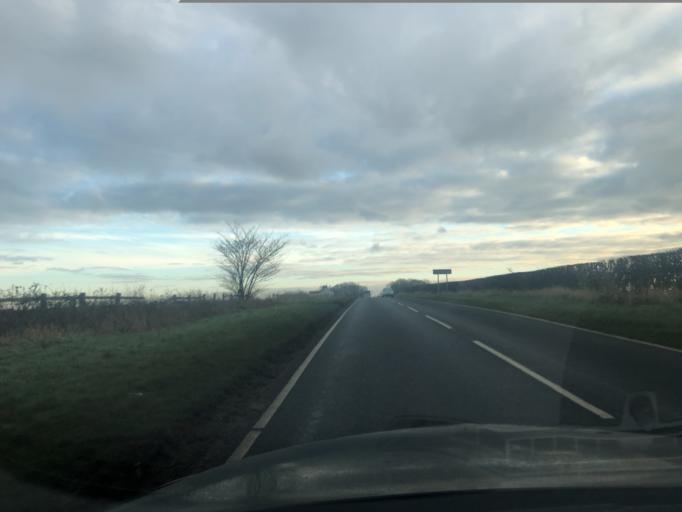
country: GB
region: England
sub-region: North Yorkshire
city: Northallerton
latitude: 54.3453
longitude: -1.4597
